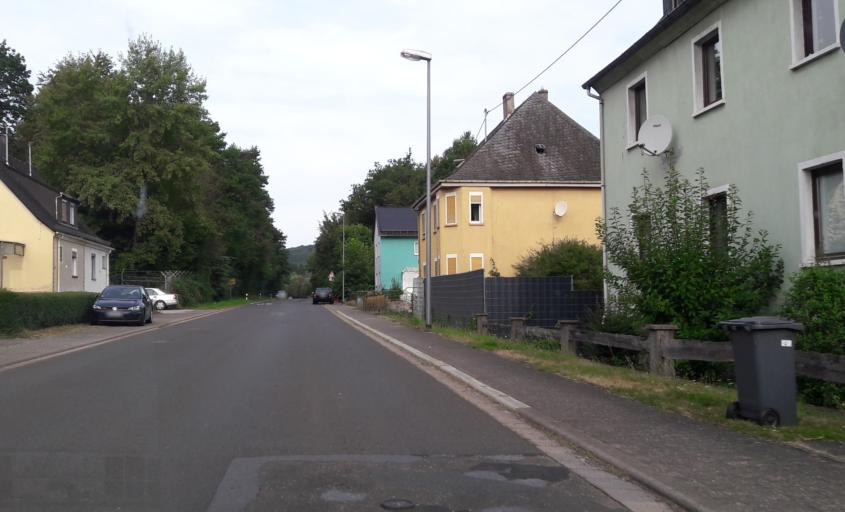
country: DE
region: Rheinland-Pfalz
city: Ellweiler
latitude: 49.6090
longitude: 7.1741
